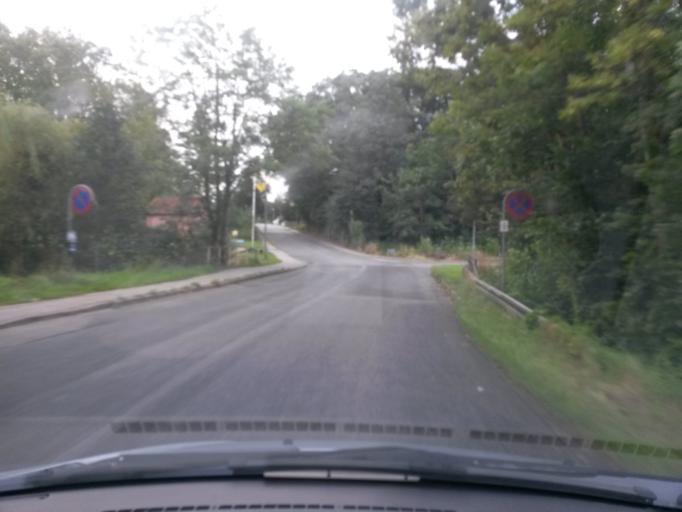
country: DK
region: Central Jutland
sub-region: Silkeborg Kommune
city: Kjellerup
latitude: 56.2917
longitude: 9.4370
